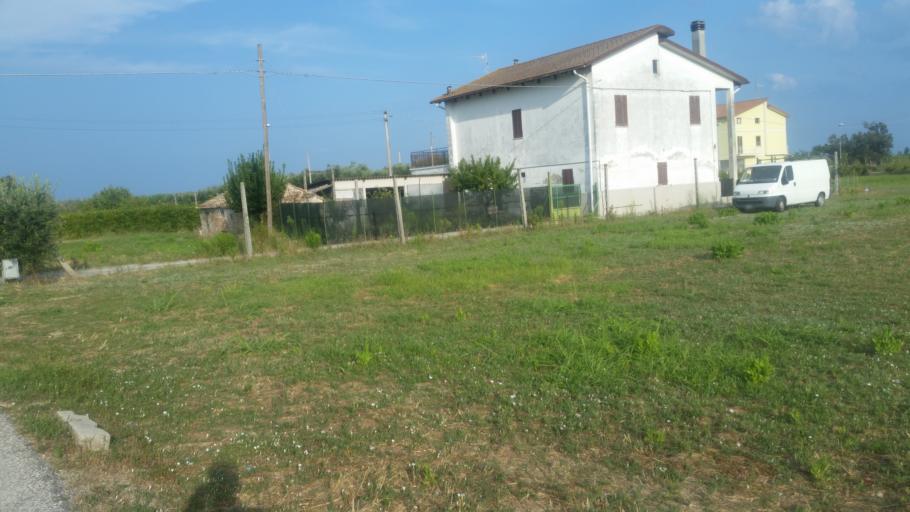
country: IT
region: The Marches
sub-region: Provincia di Ascoli Piceno
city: San Benedetto del Tronto
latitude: 42.9056
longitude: 13.9033
